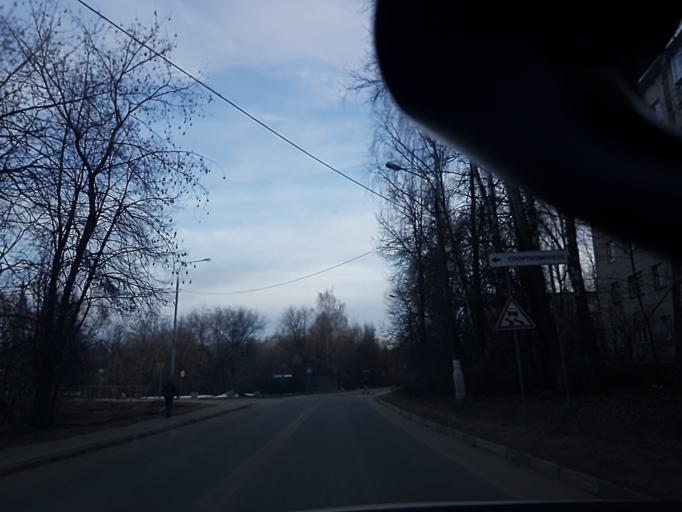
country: RU
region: Moskovskaya
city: Istra
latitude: 55.9061
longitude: 36.8678
